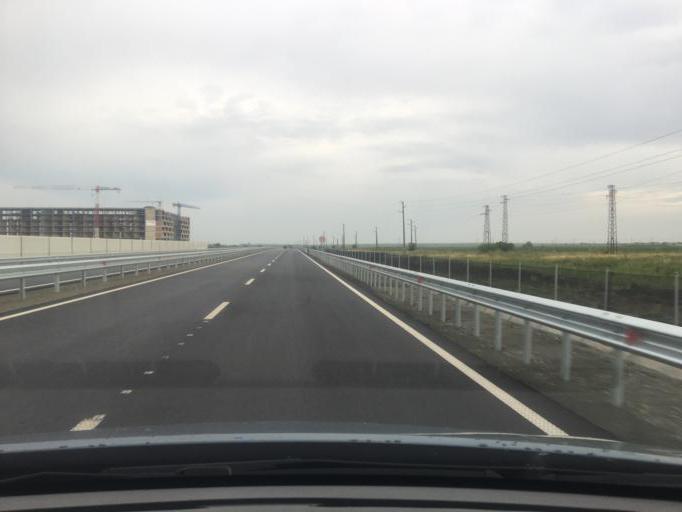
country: BG
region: Burgas
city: Aheloy
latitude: 42.6304
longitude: 27.6336
